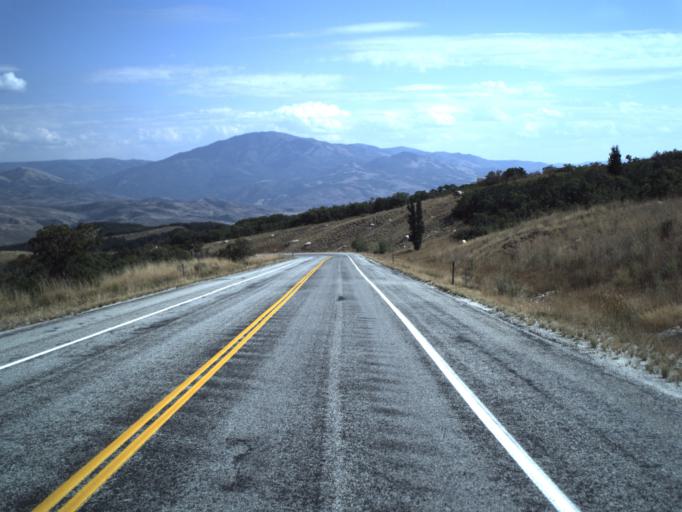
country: US
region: Utah
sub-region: Morgan County
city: Mountain Green
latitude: 41.2099
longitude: -111.8420
